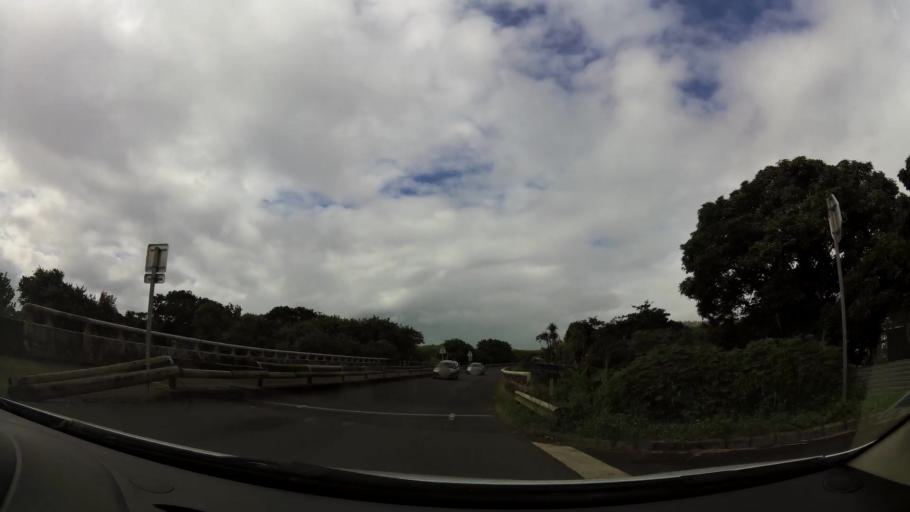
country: RE
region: Reunion
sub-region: Reunion
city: Sainte-Marie
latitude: -20.8937
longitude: 55.5548
